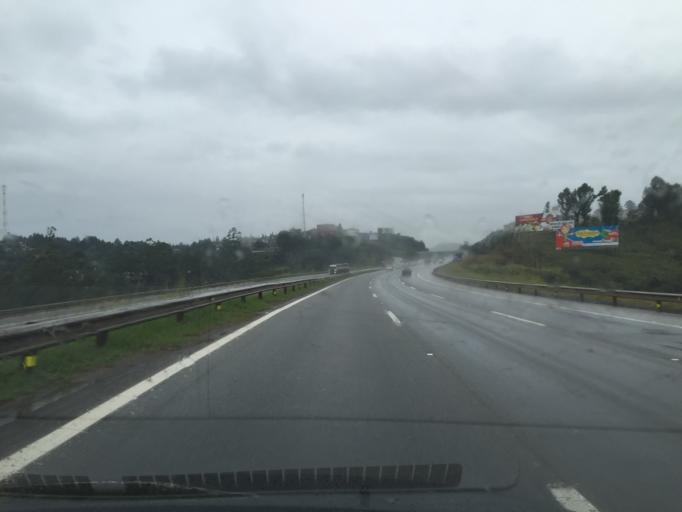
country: BR
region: Sao Paulo
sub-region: Sao Roque
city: Sao Roque
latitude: -23.4235
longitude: -47.1502
